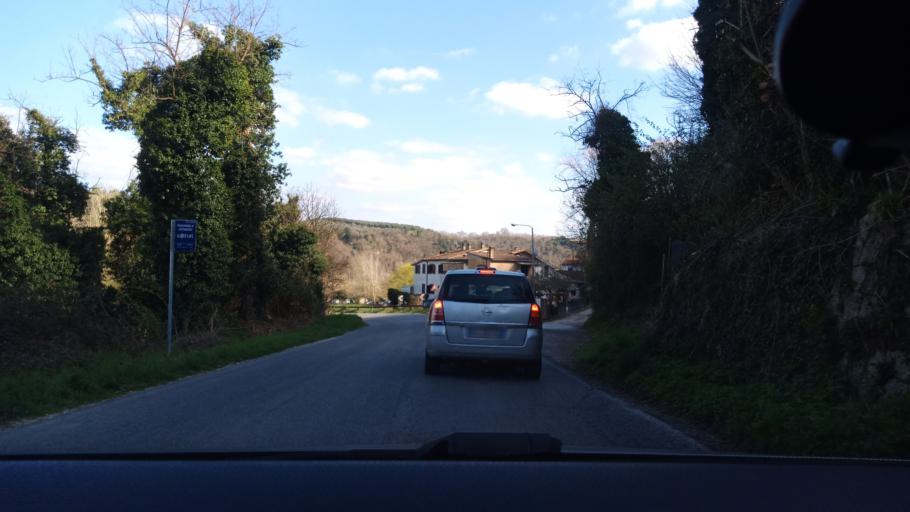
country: IT
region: Latium
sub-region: Citta metropolitana di Roma Capitale
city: Torrita Tiberina
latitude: 42.2360
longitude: 12.6265
